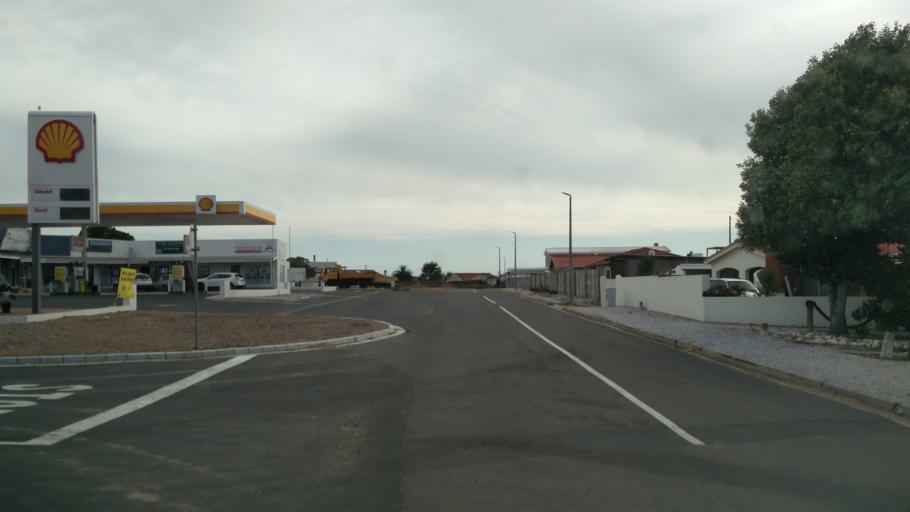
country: ZA
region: Western Cape
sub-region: City of Cape Town
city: Atlantis
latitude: -33.3453
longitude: 18.1615
